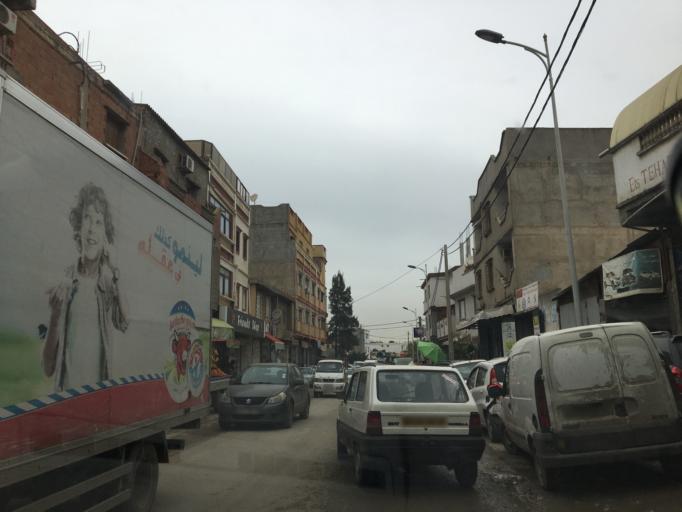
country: DZ
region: Alger
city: Rouiba
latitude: 36.7627
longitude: 3.2483
